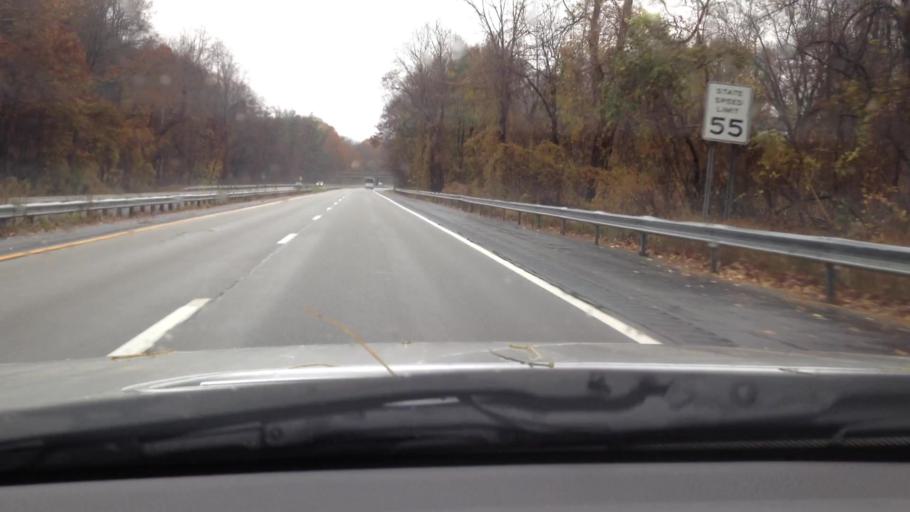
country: US
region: New York
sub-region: Westchester County
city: Crugers
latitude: 41.2398
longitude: -73.9157
